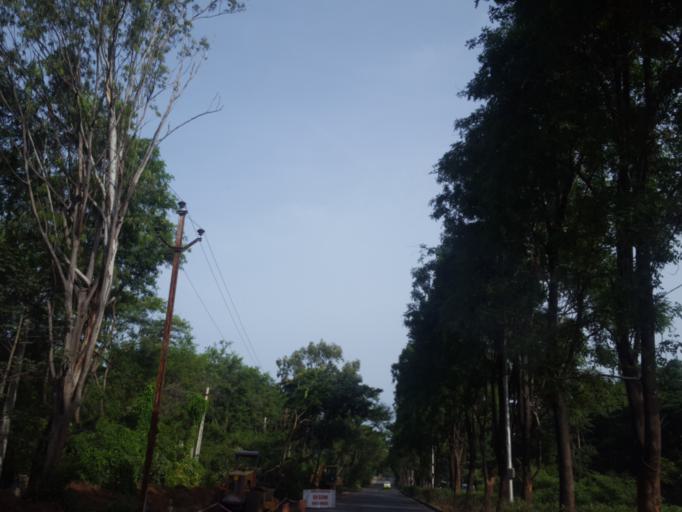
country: IN
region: Telangana
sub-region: Medak
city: Serilingampalle
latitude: 17.4547
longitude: 78.3419
